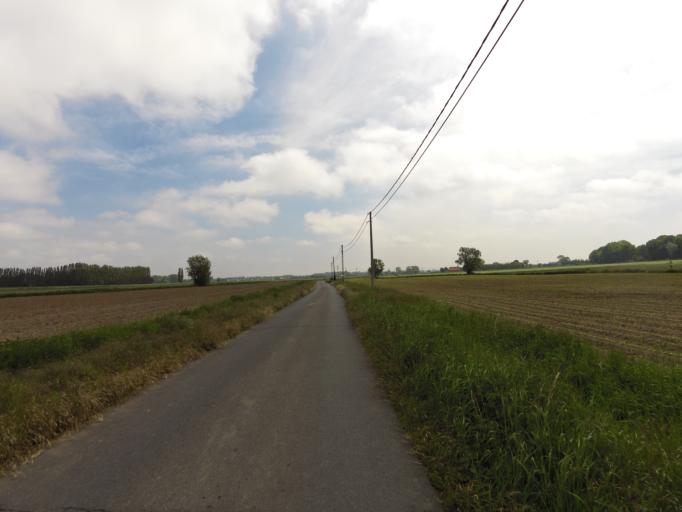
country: BE
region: Flanders
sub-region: Provincie West-Vlaanderen
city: Gistel
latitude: 51.1255
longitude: 2.9812
